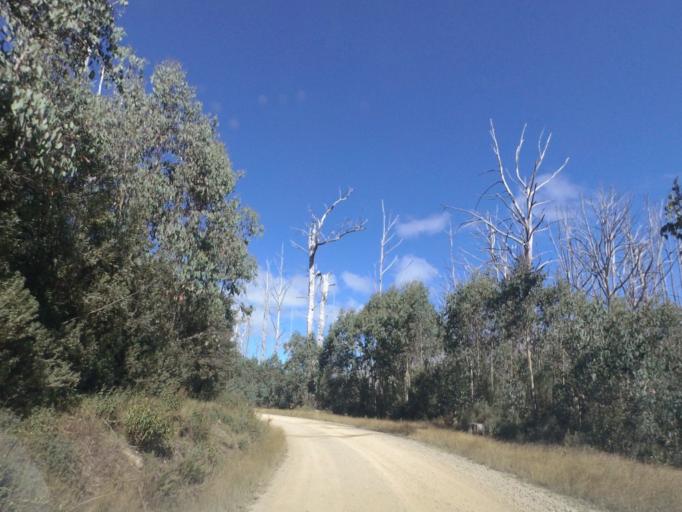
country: AU
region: Victoria
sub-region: Murrindindi
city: Alexandra
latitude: -37.4336
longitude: 145.8035
